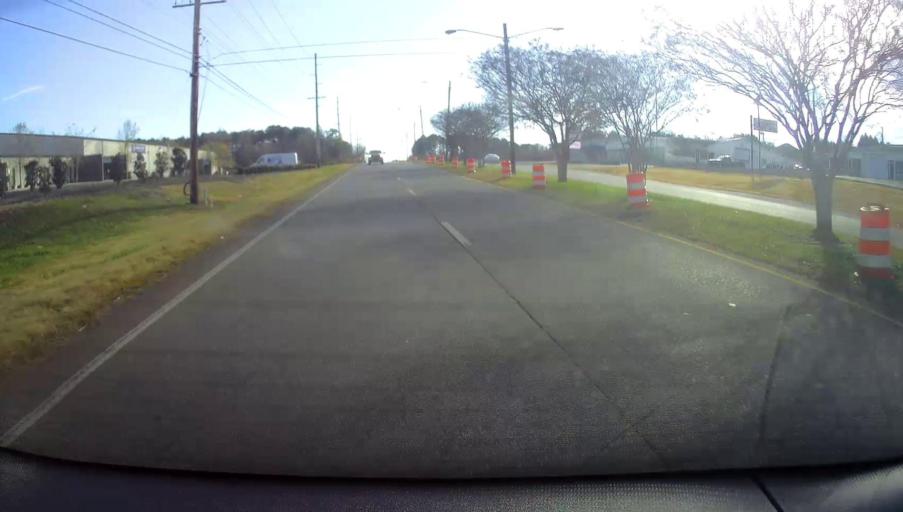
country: US
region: Alabama
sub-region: Limestone County
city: Athens
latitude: 34.7821
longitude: -86.9568
